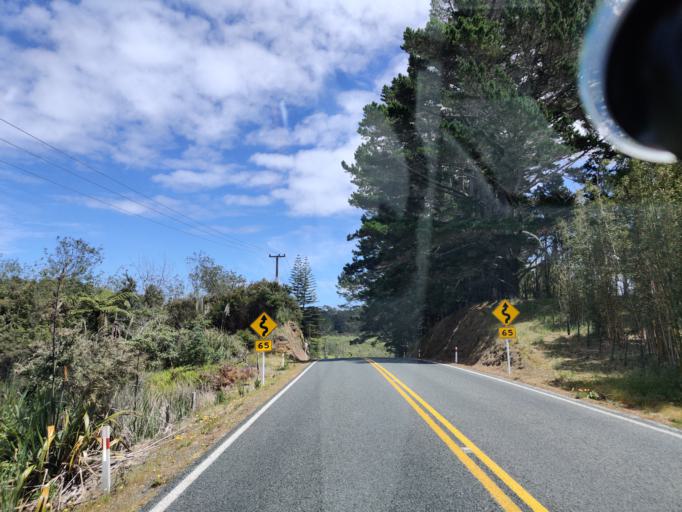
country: NZ
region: Northland
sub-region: Far North District
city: Kaitaia
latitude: -35.0067
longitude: 173.1964
